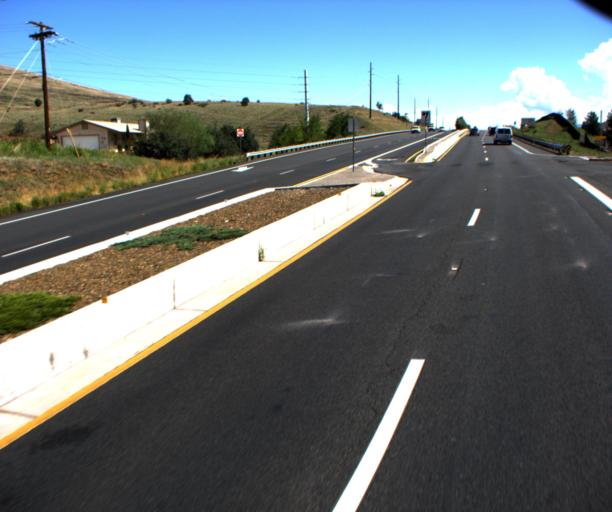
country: US
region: Arizona
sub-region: Yavapai County
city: Prescott Valley
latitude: 34.5711
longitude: -112.3696
